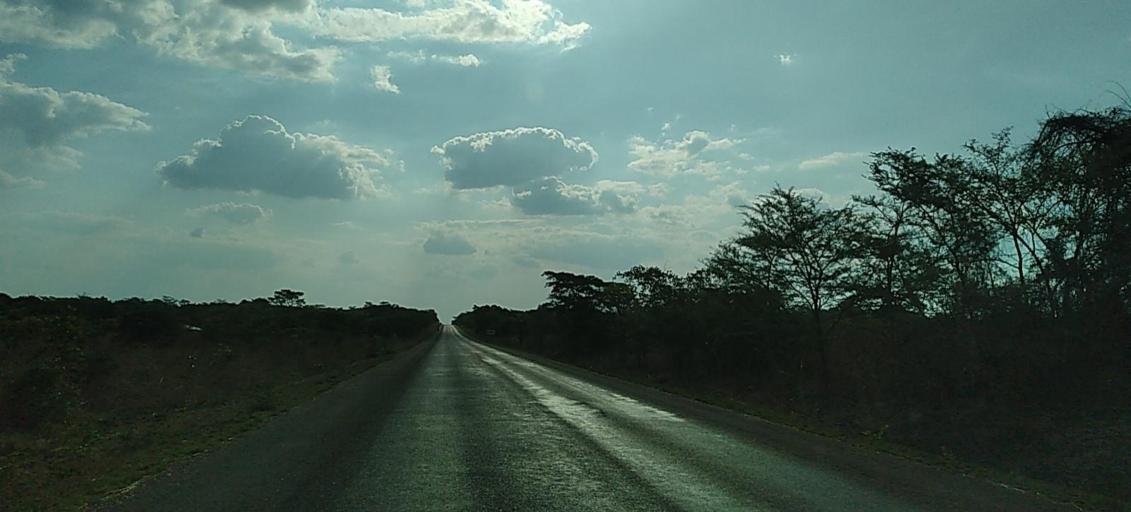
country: ZM
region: Copperbelt
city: Mpongwe
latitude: -13.3917
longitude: 28.3683
